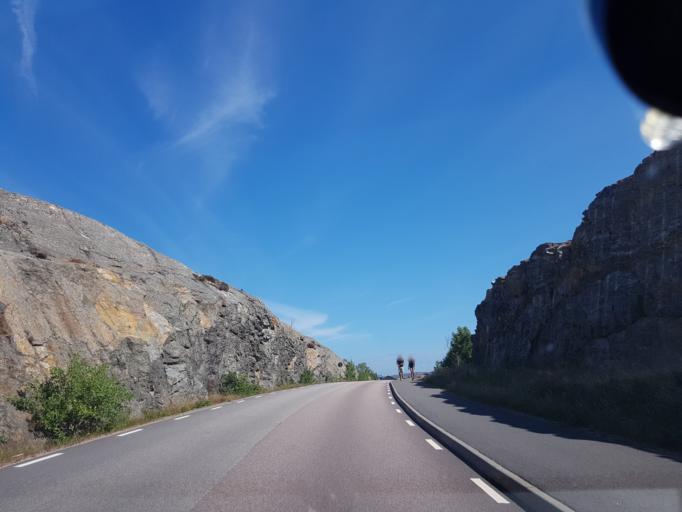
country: SE
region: Vaestra Goetaland
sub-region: Lysekils Kommun
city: Lysekil
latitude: 58.1724
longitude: 11.4158
